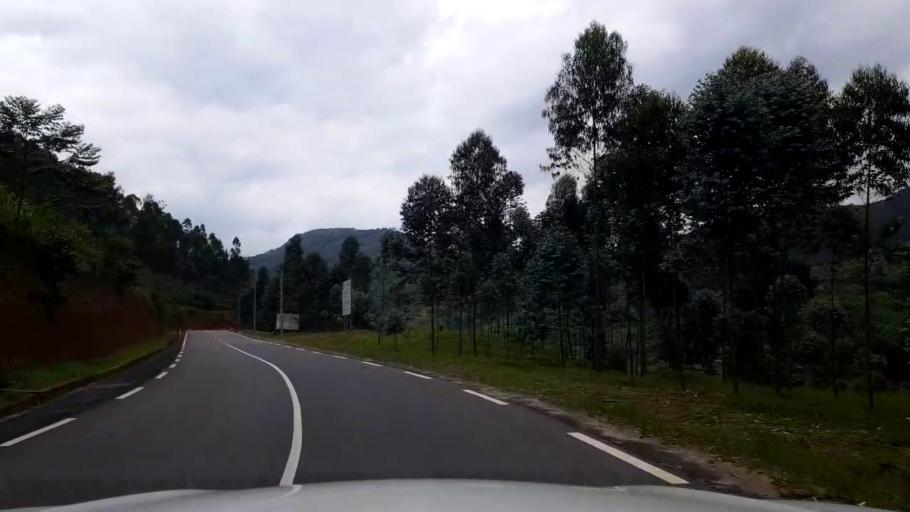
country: RW
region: Western Province
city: Kibuye
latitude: -1.9208
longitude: 29.3697
